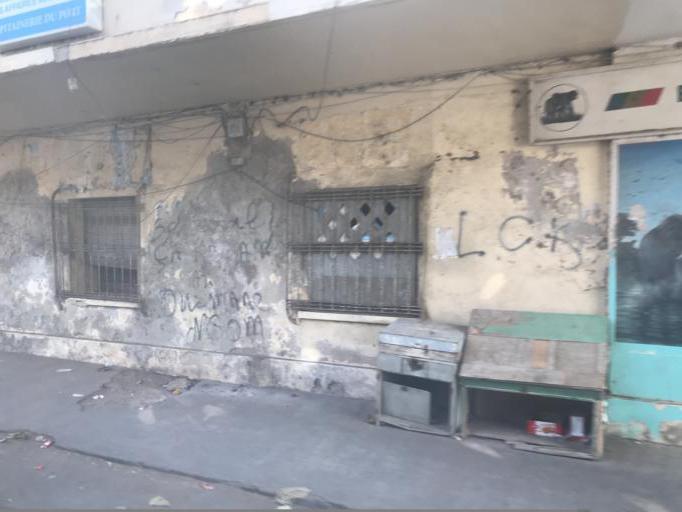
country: SN
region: Saint-Louis
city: Saint-Louis
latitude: 16.0249
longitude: -16.5041
